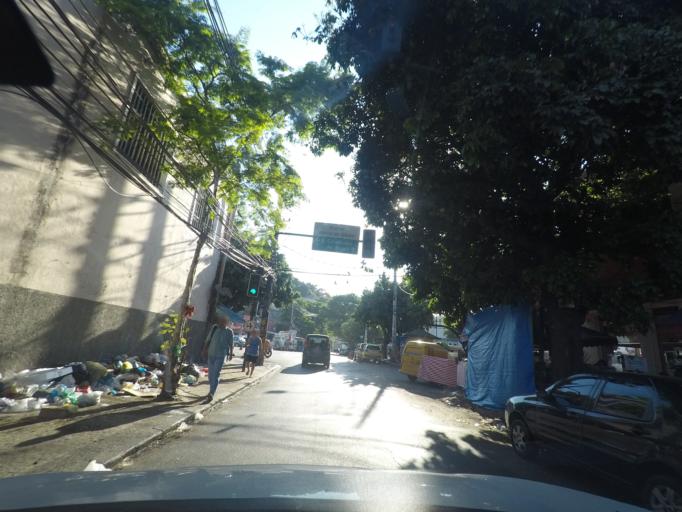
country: BR
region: Rio de Janeiro
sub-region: Rio De Janeiro
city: Rio de Janeiro
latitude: -22.8897
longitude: -43.2289
